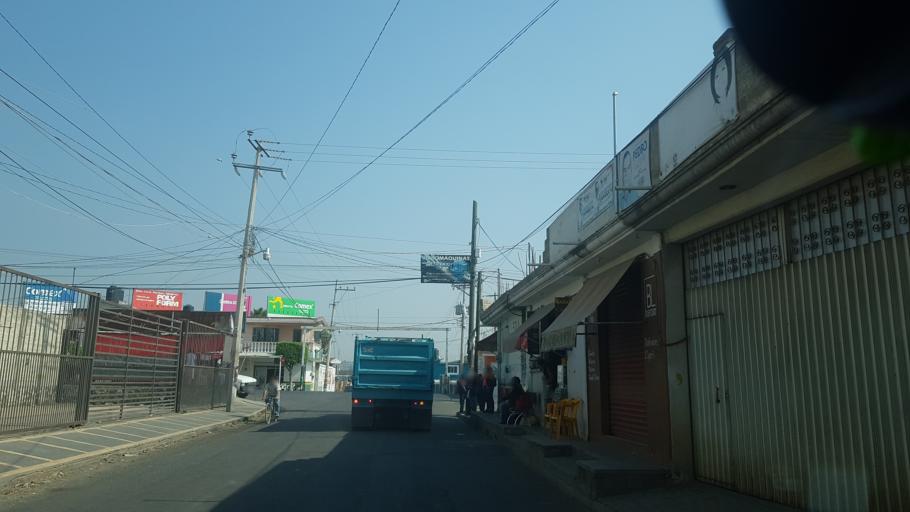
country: MX
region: Puebla
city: Nealtican
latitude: 19.0541
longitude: -98.4213
